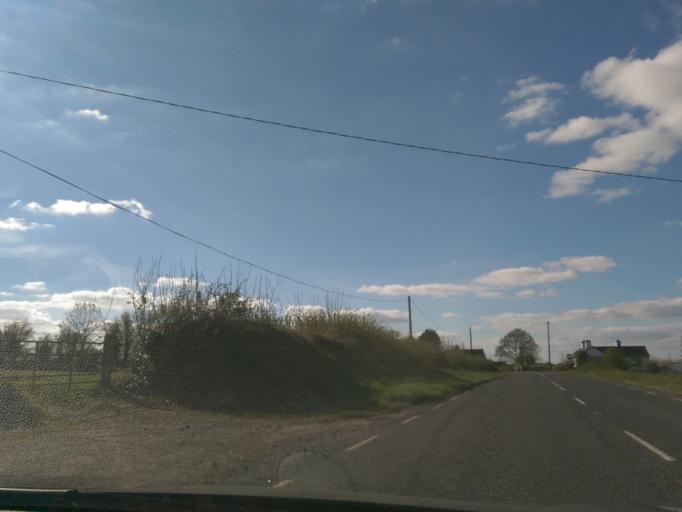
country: IE
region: Leinster
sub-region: Uibh Fhaili
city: Birr
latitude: 53.0949
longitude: -7.9666
